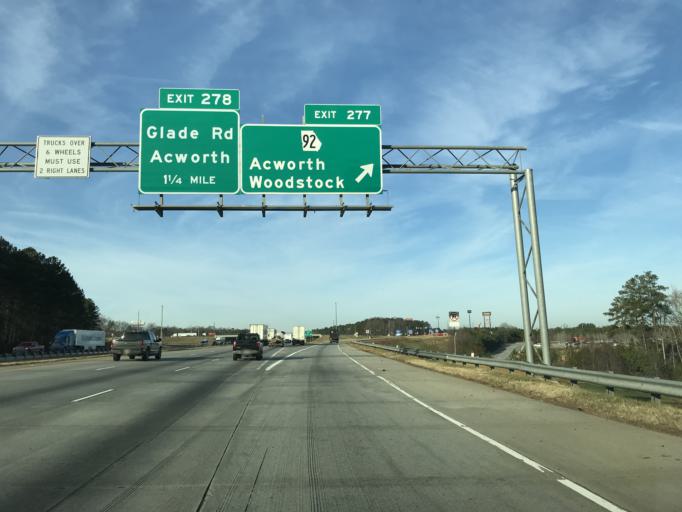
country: US
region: Georgia
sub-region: Cobb County
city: Acworth
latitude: 34.0794
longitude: -84.6478
